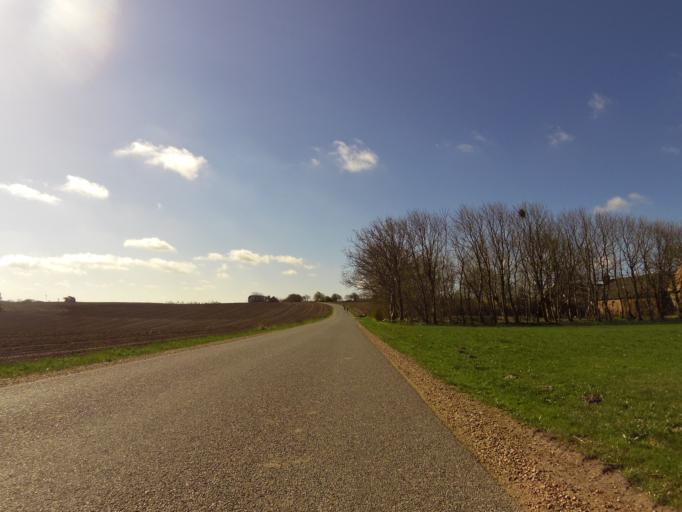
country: DK
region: Central Jutland
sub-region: Holstebro Kommune
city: Vinderup
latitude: 56.4605
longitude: 8.7219
